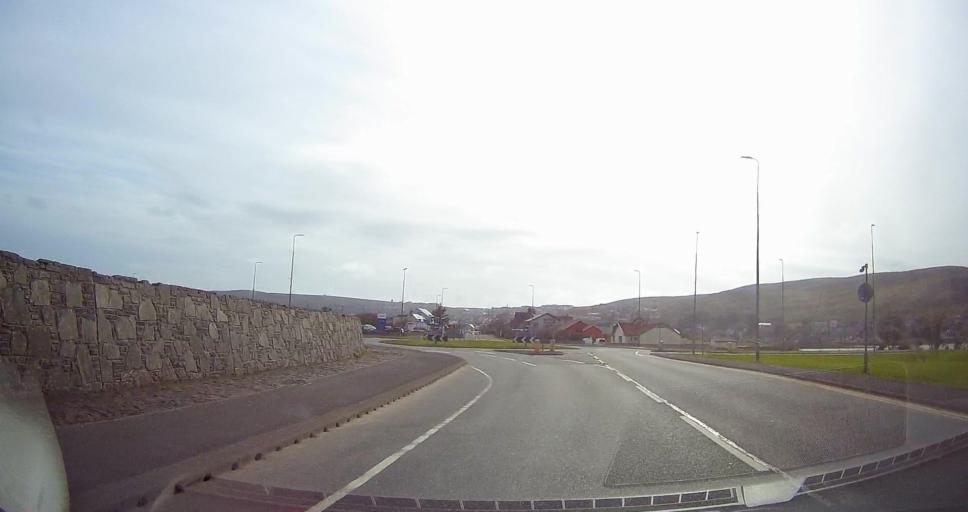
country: GB
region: Scotland
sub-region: Shetland Islands
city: Lerwick
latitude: 60.1491
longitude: -1.1585
